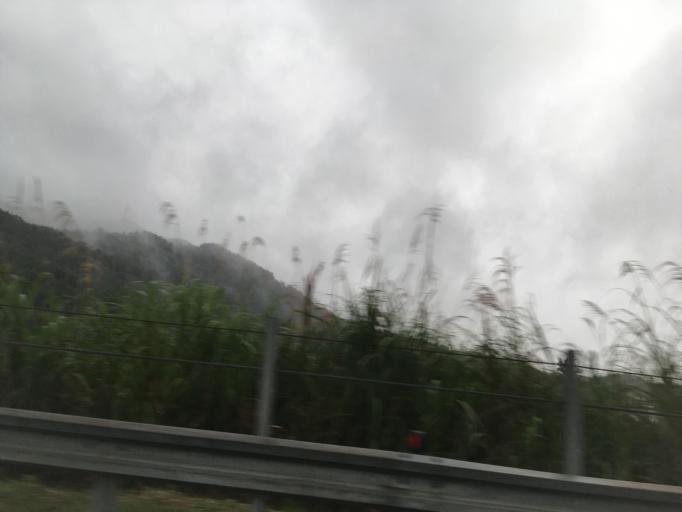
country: TW
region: Taiwan
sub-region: Keelung
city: Keelung
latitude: 25.0354
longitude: 121.8565
